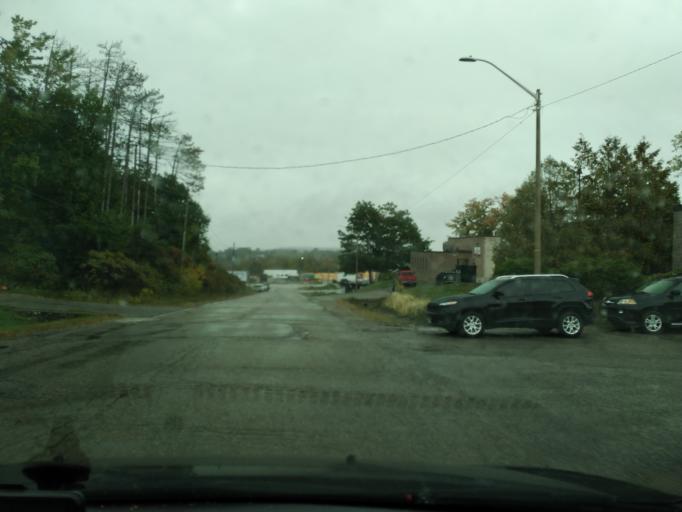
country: CA
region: Ontario
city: Barrie
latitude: 44.3574
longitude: -79.6716
